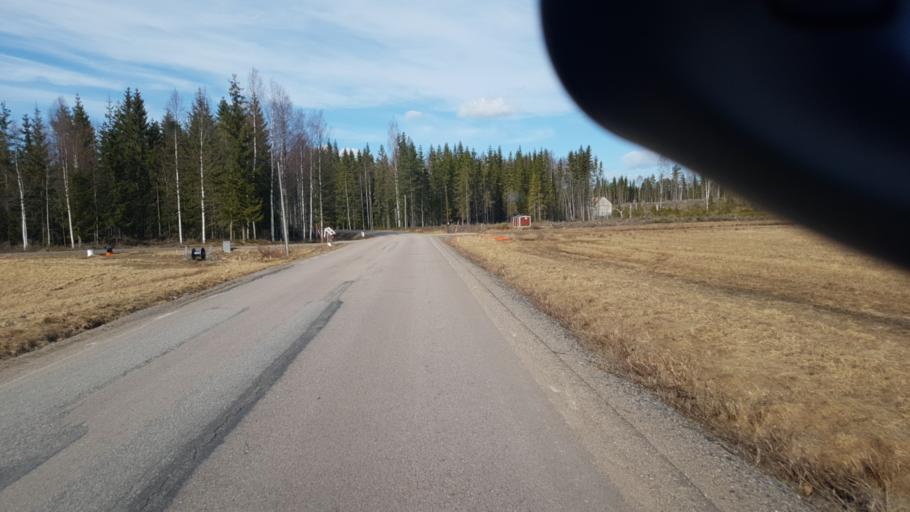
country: SE
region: Vaermland
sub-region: Eda Kommun
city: Charlottenberg
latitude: 59.8743
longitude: 12.3503
